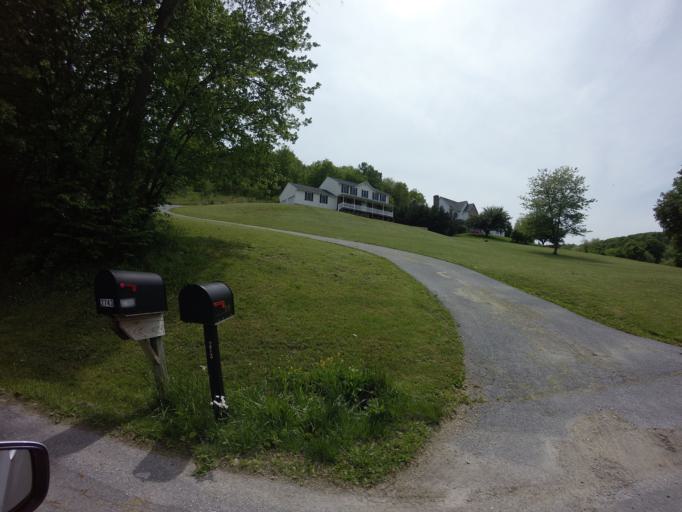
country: US
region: Maryland
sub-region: Carroll County
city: New Windsor
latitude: 39.4797
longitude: -77.0954
